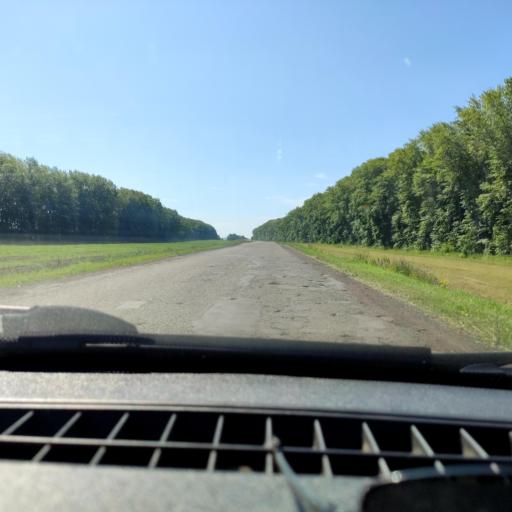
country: RU
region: Bashkortostan
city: Karmaskaly
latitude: 54.3947
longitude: 56.1706
